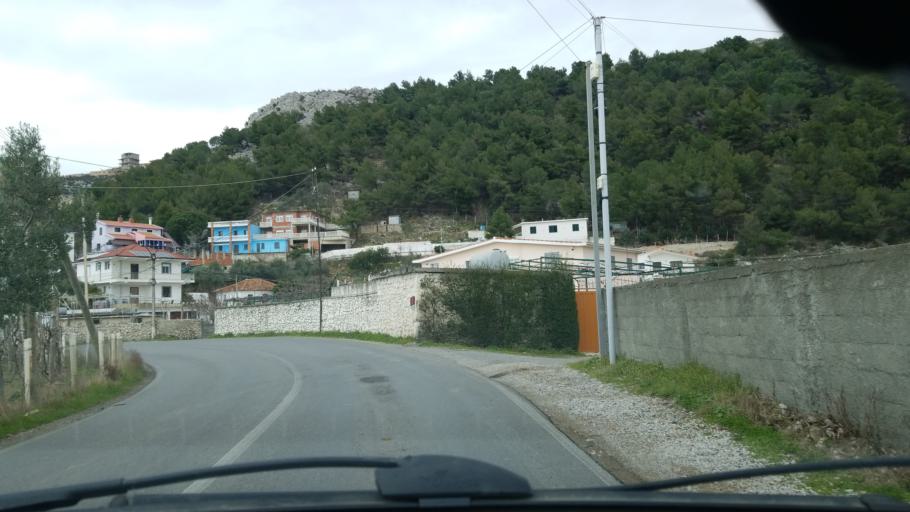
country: AL
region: Lezhe
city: Lezhe
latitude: 41.7870
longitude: 19.6282
